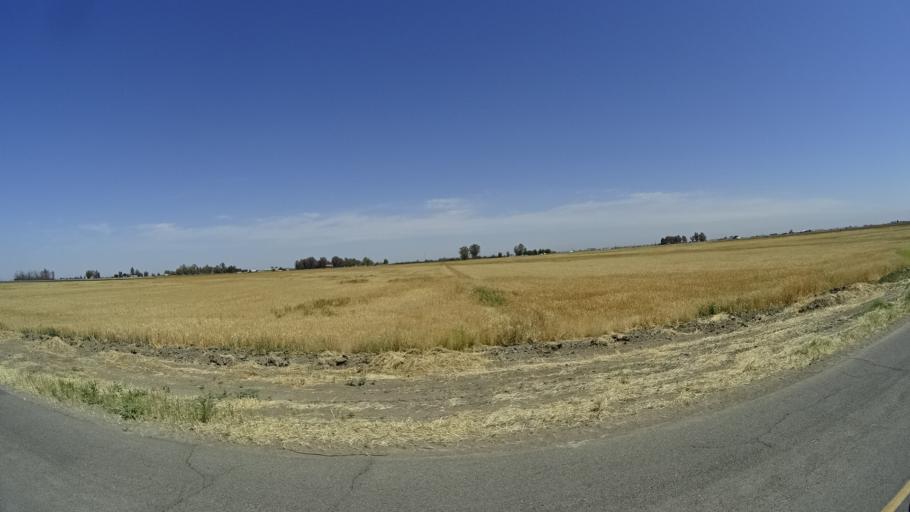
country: US
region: California
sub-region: Kings County
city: Stratford
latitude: 36.1887
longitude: -119.7869
